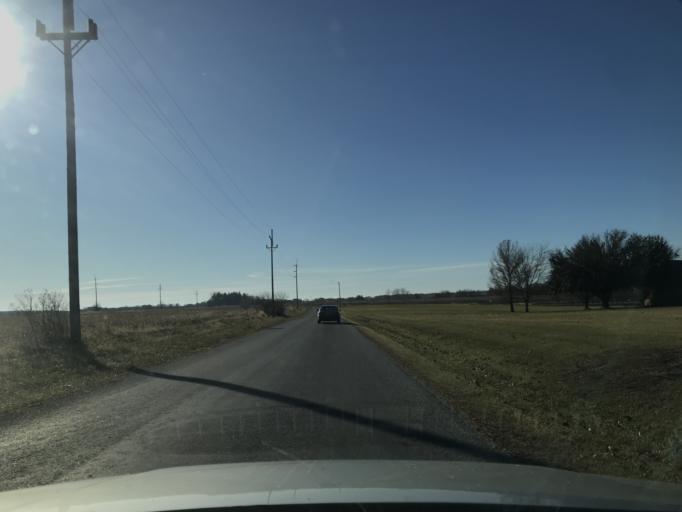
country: US
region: Illinois
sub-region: Hancock County
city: Carthage
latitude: 40.4633
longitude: -91.1784
